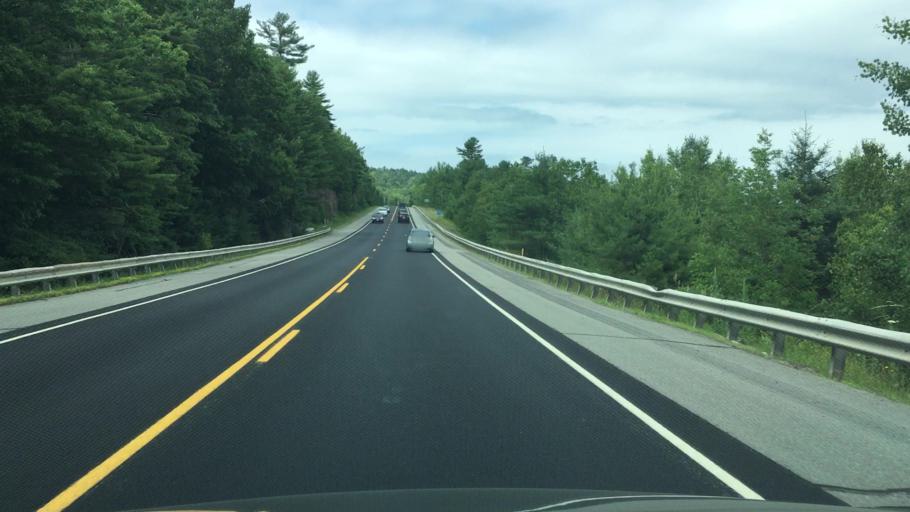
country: US
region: Maine
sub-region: Hancock County
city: Bucksport
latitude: 44.5473
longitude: -68.8091
